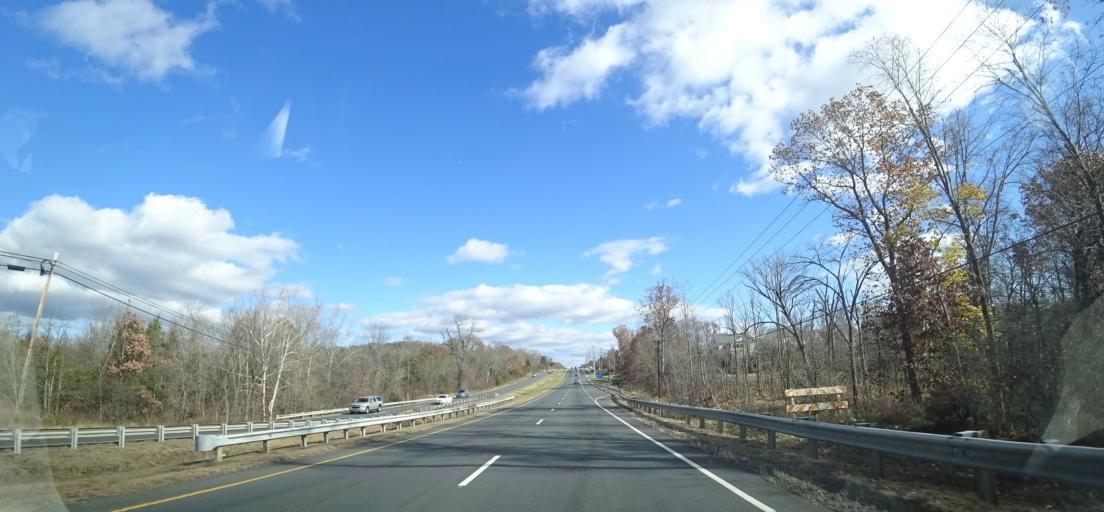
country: US
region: Virginia
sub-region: Prince William County
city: Haymarket
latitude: 38.7843
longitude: -77.6585
